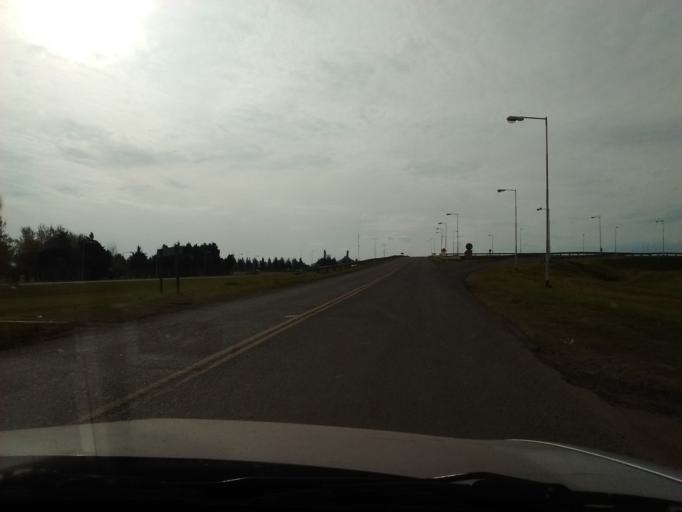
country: AR
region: Santa Fe
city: Funes
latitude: -32.9426
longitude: -60.8197
